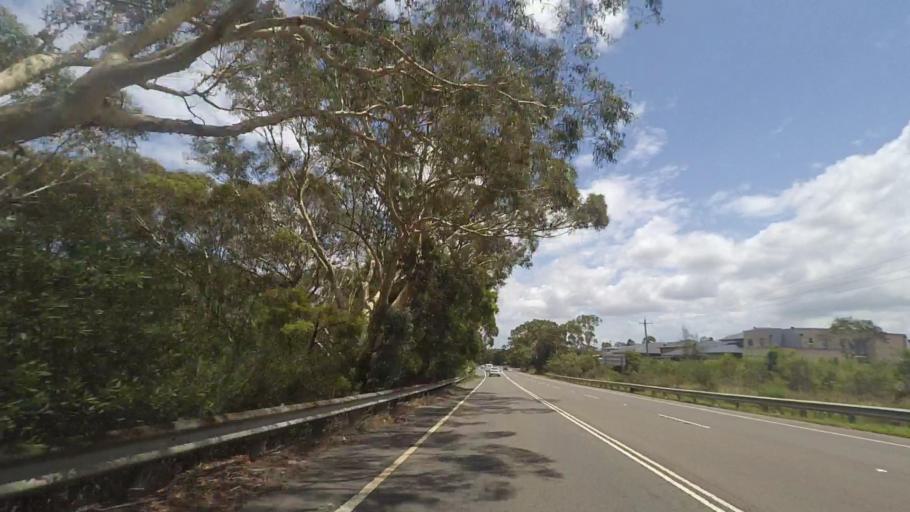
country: AU
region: New South Wales
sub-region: Liverpool
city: East Hills
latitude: -33.9677
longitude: 150.9732
